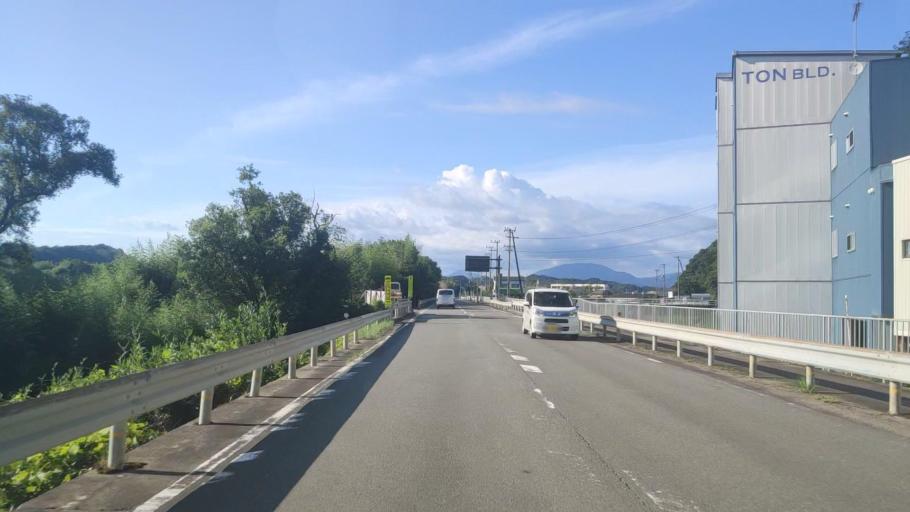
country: JP
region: Wakayama
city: Tanabe
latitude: 33.6692
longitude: 135.4081
